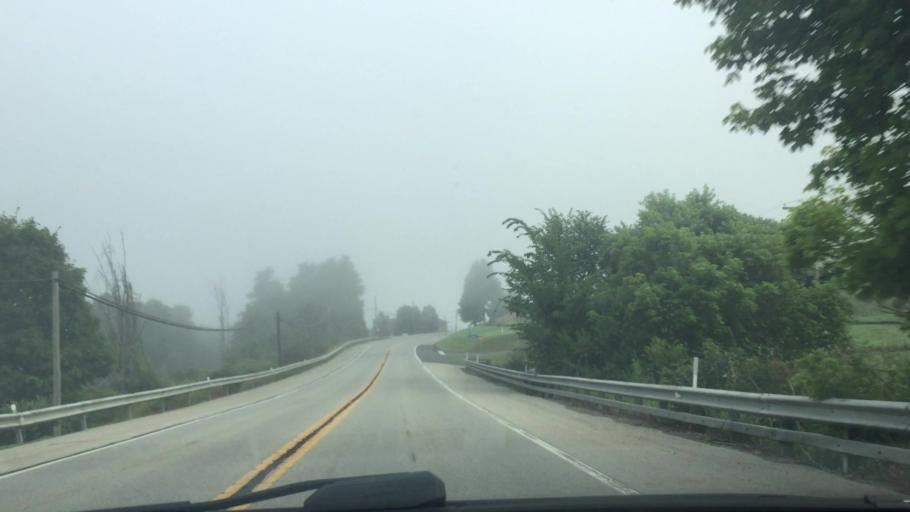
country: US
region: Pennsylvania
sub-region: Washington County
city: McGovern
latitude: 40.1860
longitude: -80.1339
